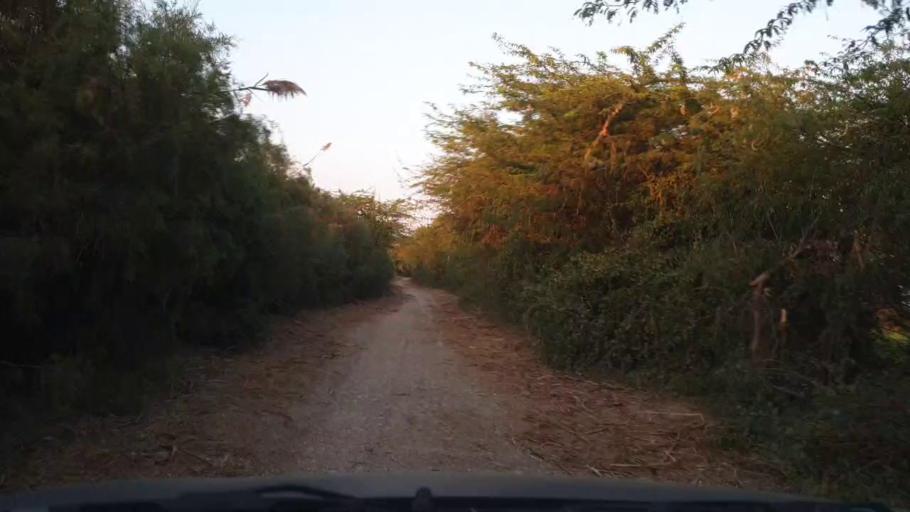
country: PK
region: Sindh
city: Jhol
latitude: 25.9202
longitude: 68.9621
